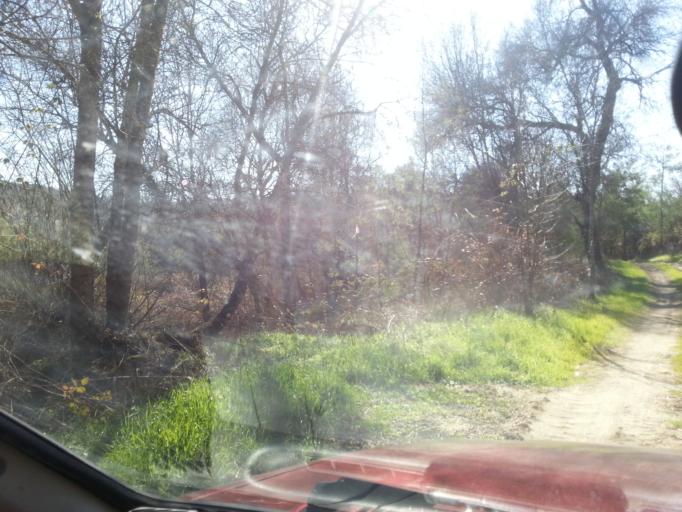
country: PT
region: Guarda
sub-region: Fornos de Algodres
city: Fornos de Algodres
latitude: 40.6141
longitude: -7.5171
